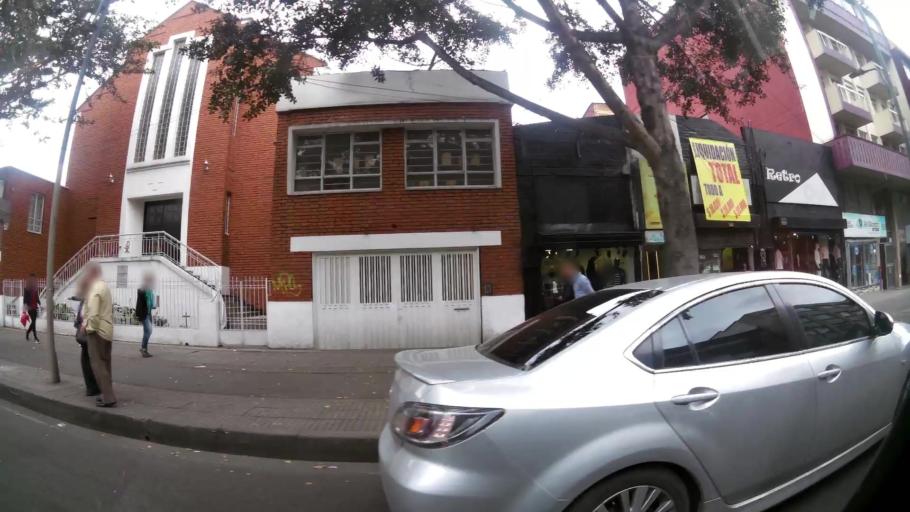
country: CO
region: Bogota D.C.
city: Bogota
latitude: 4.6427
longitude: -74.0647
